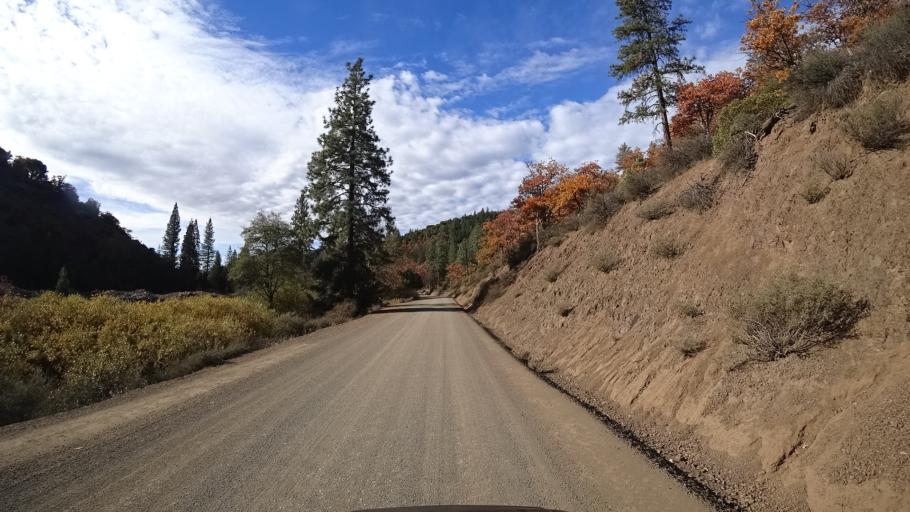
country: US
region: California
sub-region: Siskiyou County
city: Yreka
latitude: 41.7102
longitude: -122.8123
